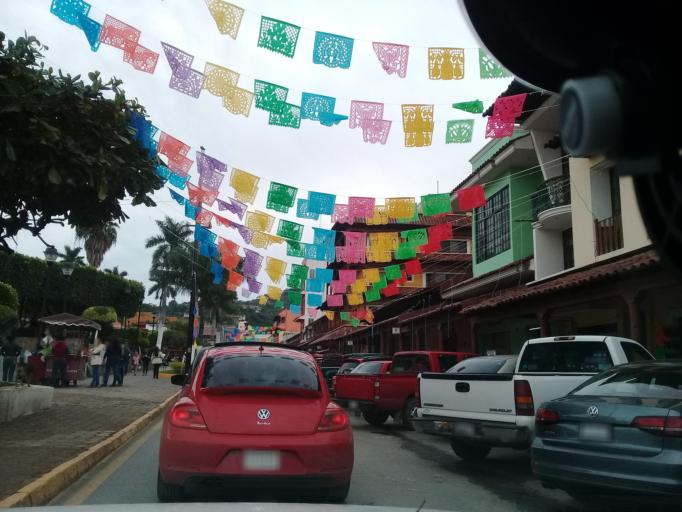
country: MX
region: Hidalgo
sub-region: Huejutla de Reyes
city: Huejutla de Reyes
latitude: 21.1411
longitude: -98.4200
